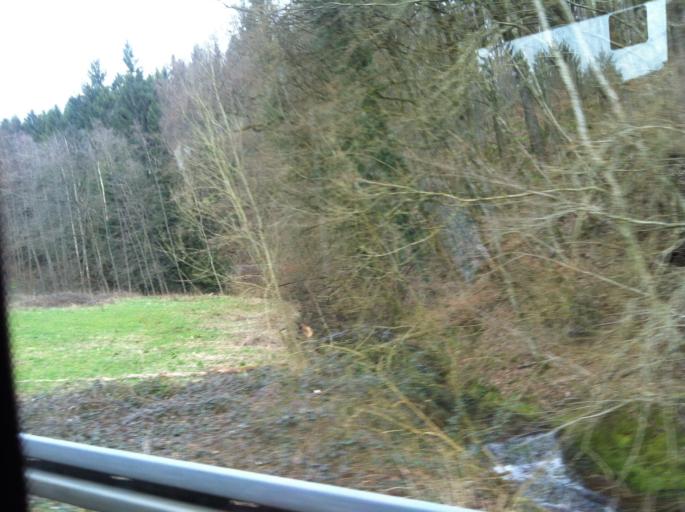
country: DE
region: Baden-Wuerttemberg
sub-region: Karlsruhe Region
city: Mosbach
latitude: 49.3923
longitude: 9.1503
